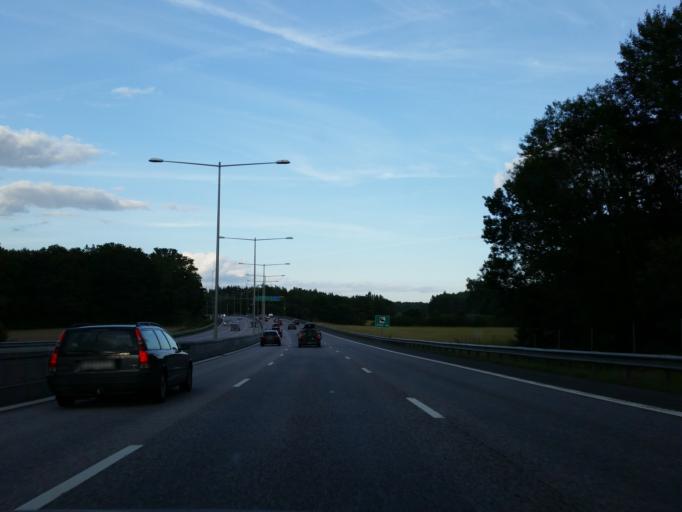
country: SE
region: Stockholm
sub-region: Salems Kommun
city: Ronninge
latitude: 59.2109
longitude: 17.7308
